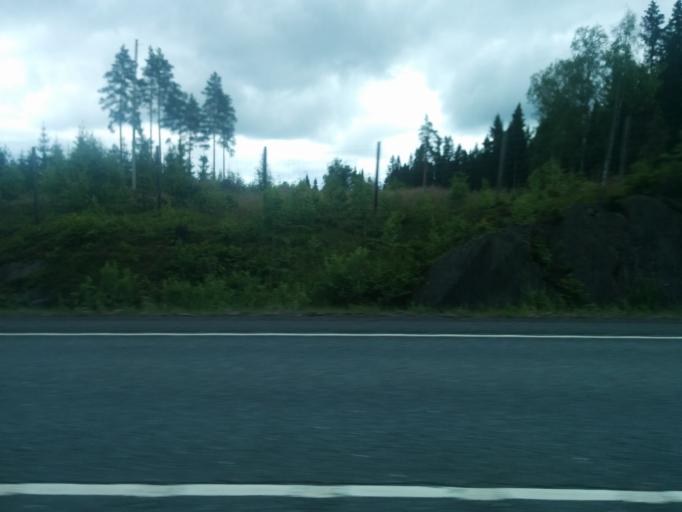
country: FI
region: Pirkanmaa
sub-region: Tampere
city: Orivesi
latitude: 61.6618
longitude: 24.2615
